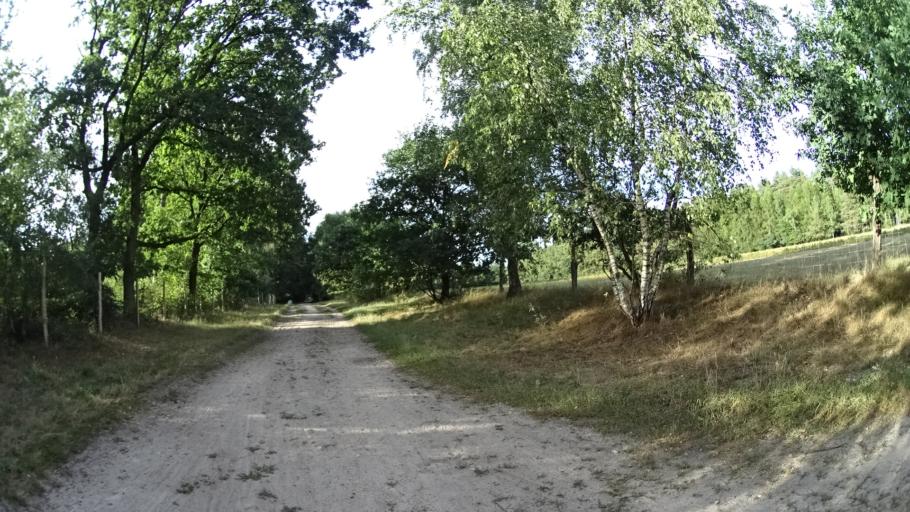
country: DE
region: Lower Saxony
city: Handeloh
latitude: 53.2108
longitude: 9.8819
